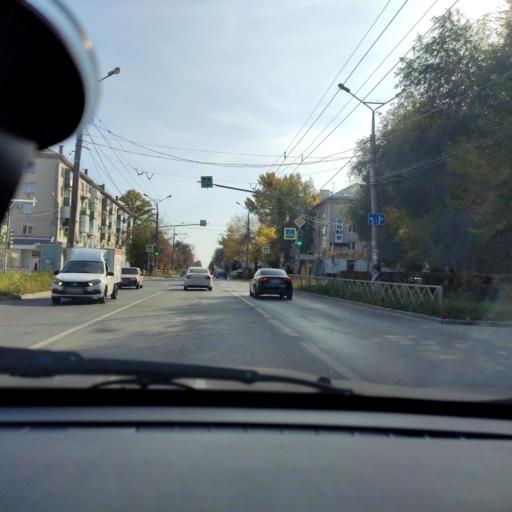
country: RU
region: Samara
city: Tol'yatti
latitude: 53.5194
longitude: 49.4157
